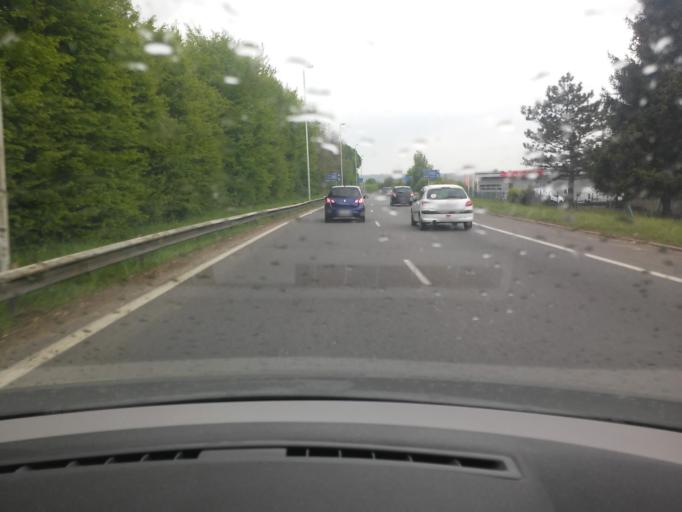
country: FR
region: Lorraine
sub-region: Departement de Meurthe-et-Moselle
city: Laxou
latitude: 48.6951
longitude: 6.1218
